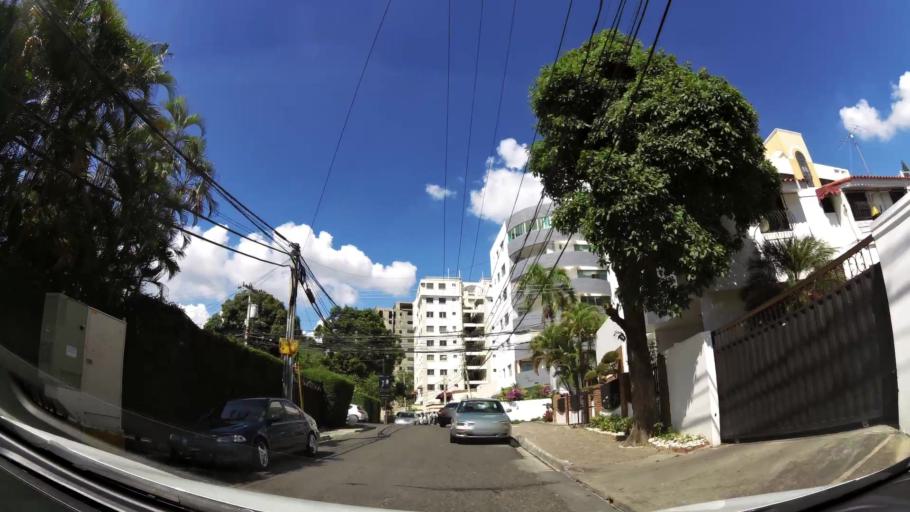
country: DO
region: Santiago
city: Santiago de los Caballeros
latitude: 19.4515
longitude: -70.6827
